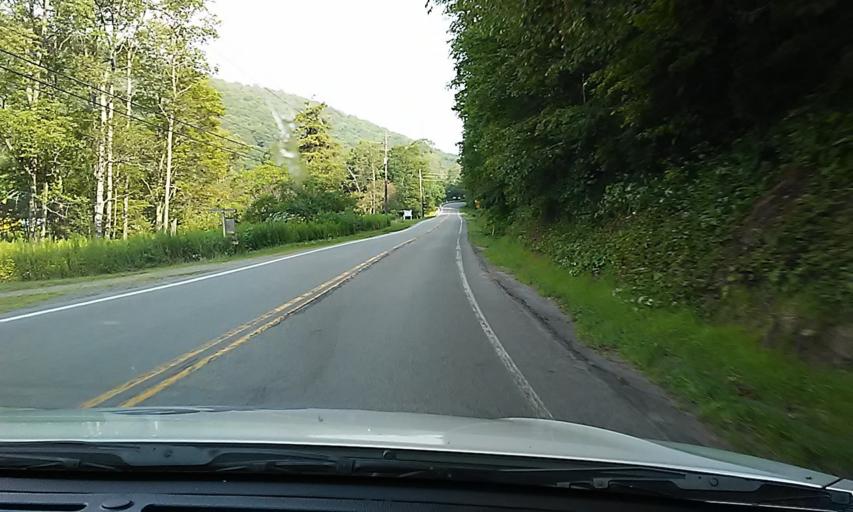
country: US
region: Pennsylvania
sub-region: Potter County
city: Galeton
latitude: 41.8087
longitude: -77.7805
